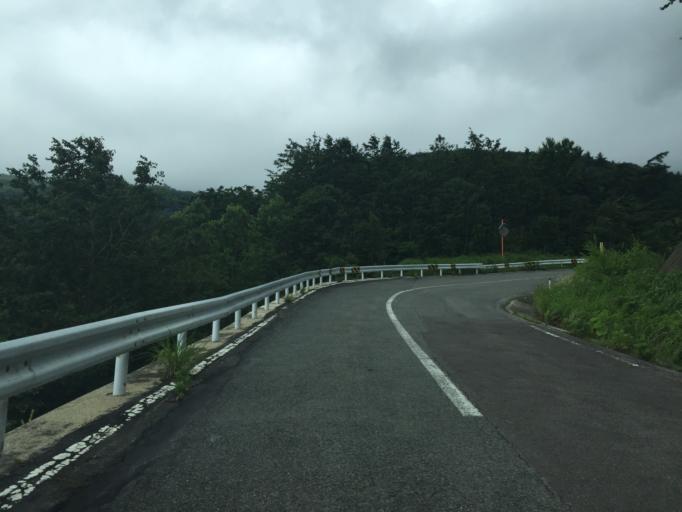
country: JP
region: Yamagata
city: Yonezawa
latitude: 37.7559
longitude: 140.1044
